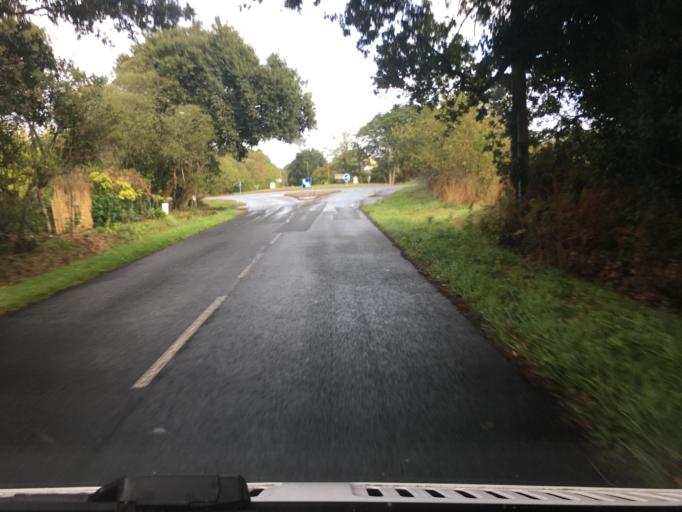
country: FR
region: Brittany
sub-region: Departement du Finistere
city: Plobannalec-Lesconil
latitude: 47.8491
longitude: -4.2153
